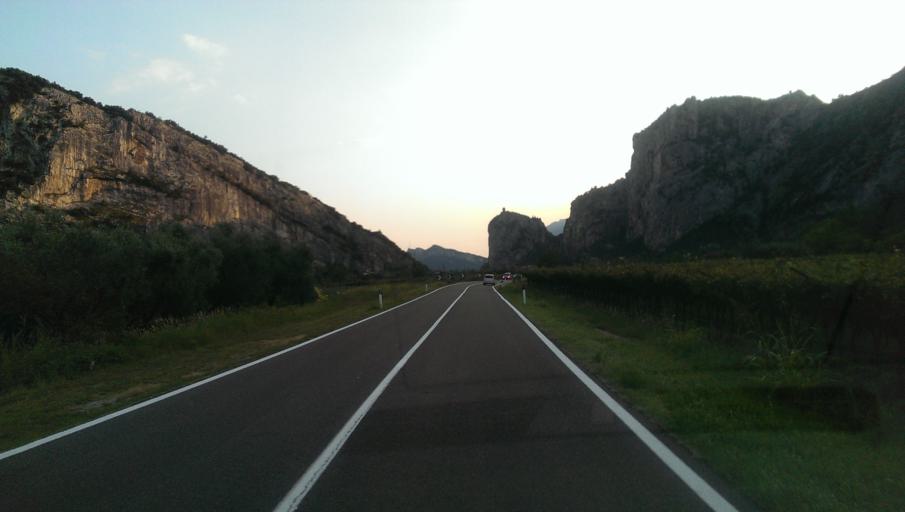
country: IT
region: Trentino-Alto Adige
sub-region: Provincia di Trento
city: Arco
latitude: 45.9385
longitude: 10.9006
